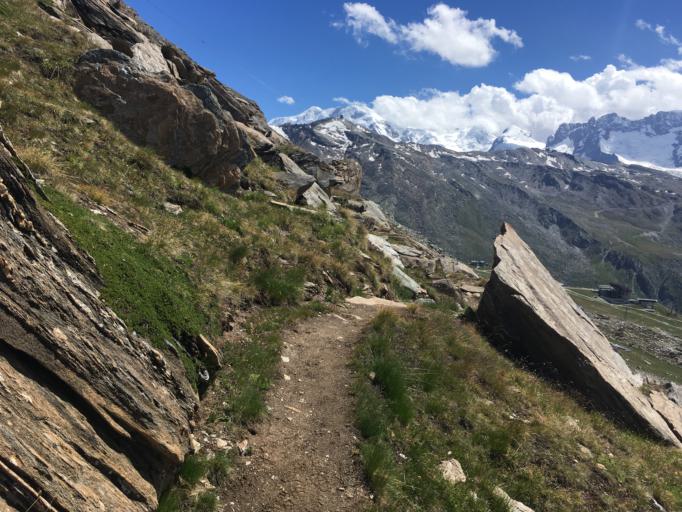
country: CH
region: Valais
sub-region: Visp District
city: Zermatt
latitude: 46.0255
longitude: 7.7882
